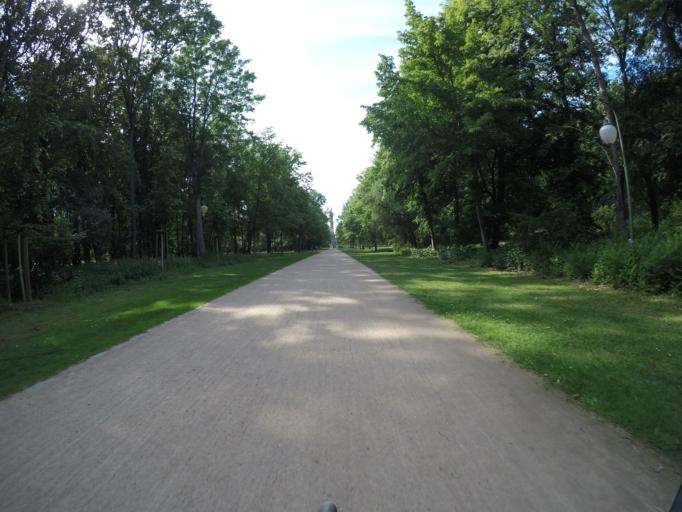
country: DE
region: Berlin
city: Tiergarten Bezirk
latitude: 52.5121
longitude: 13.3559
